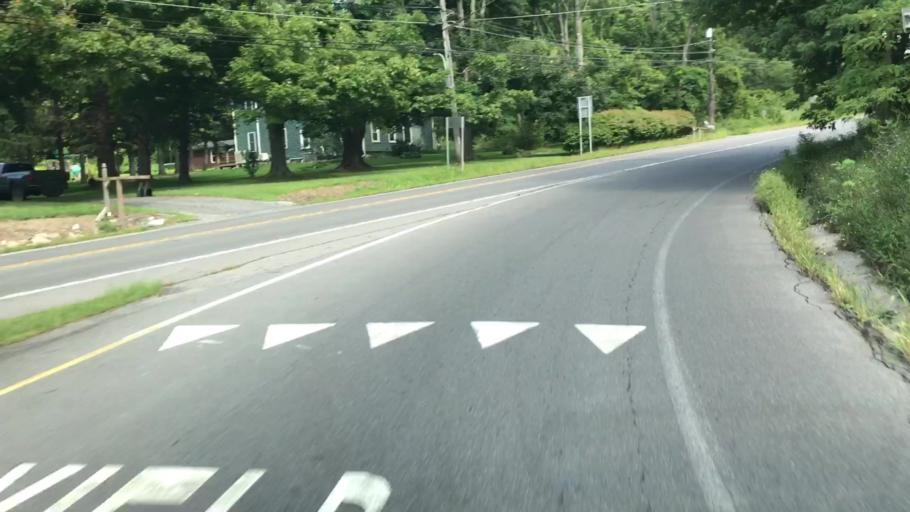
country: US
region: New York
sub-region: Onondaga County
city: Marcellus
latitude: 42.9828
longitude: -76.3308
